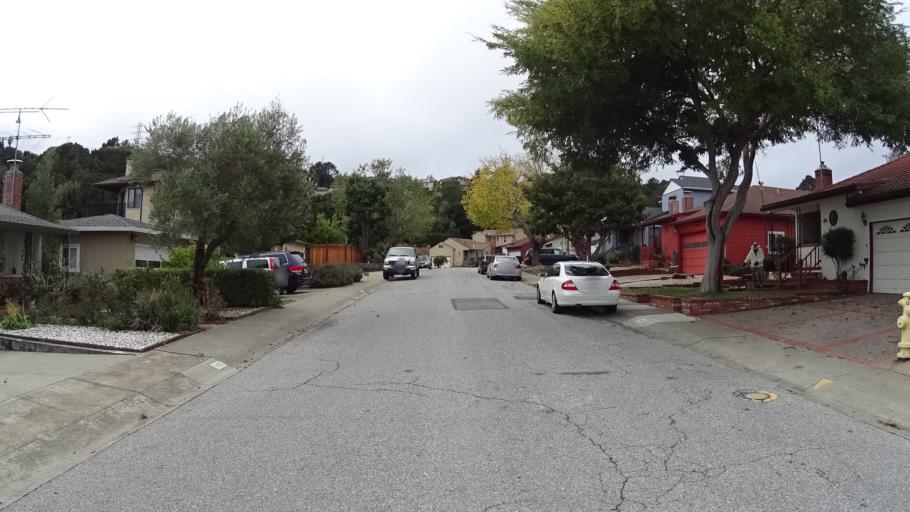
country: US
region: California
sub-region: San Mateo County
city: Millbrae
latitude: 37.6002
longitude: -122.4067
